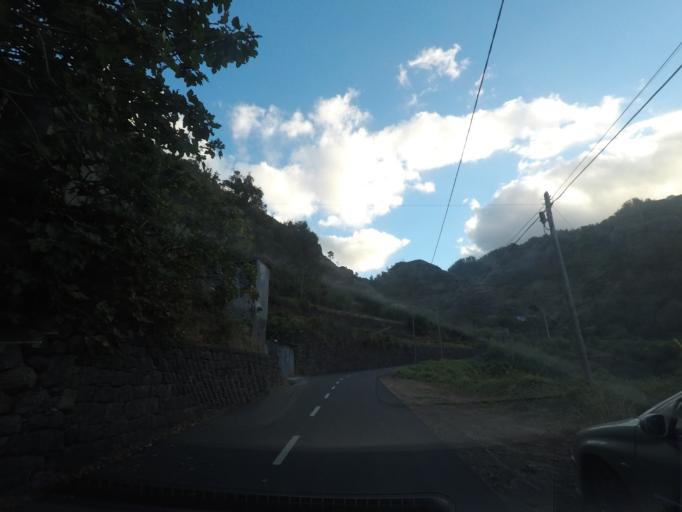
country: PT
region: Madeira
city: Ponta do Sol
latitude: 32.6914
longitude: -17.0740
